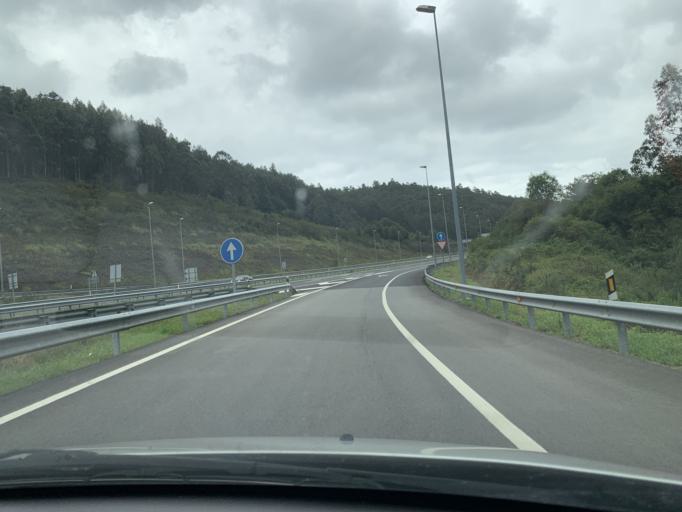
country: ES
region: Asturias
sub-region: Province of Asturias
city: Ribadesella
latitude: 43.4378
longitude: -5.0421
